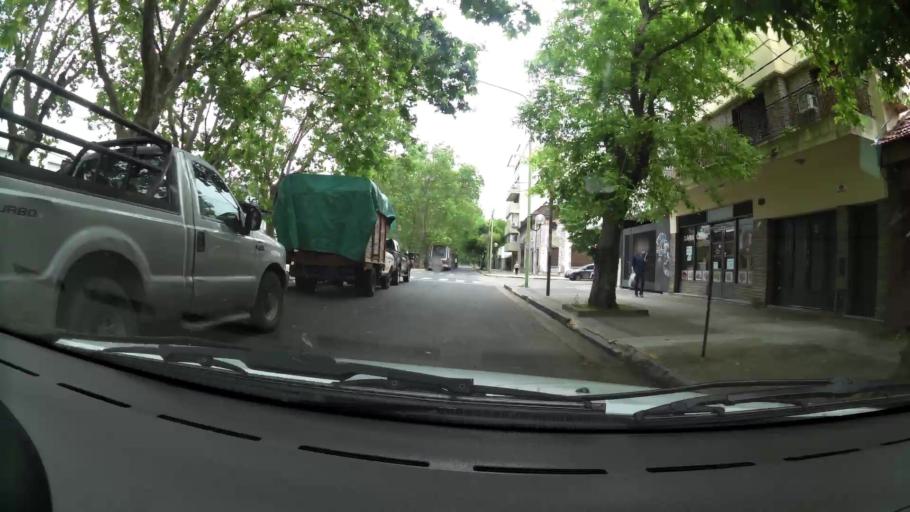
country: AR
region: Buenos Aires
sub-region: Partido de La Plata
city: La Plata
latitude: -34.9292
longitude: -57.9643
